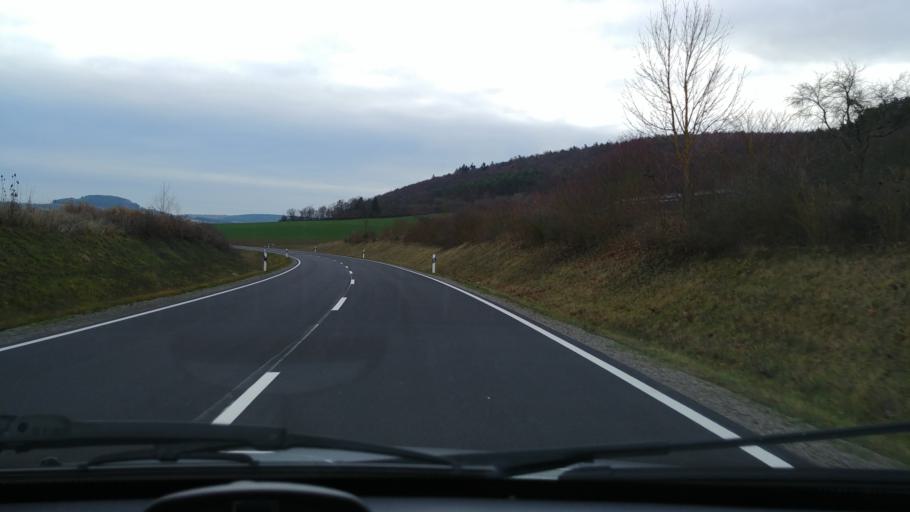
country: DE
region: Bavaria
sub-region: Regierungsbezirk Unterfranken
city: Karlstadt
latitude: 49.9744
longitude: 9.7437
